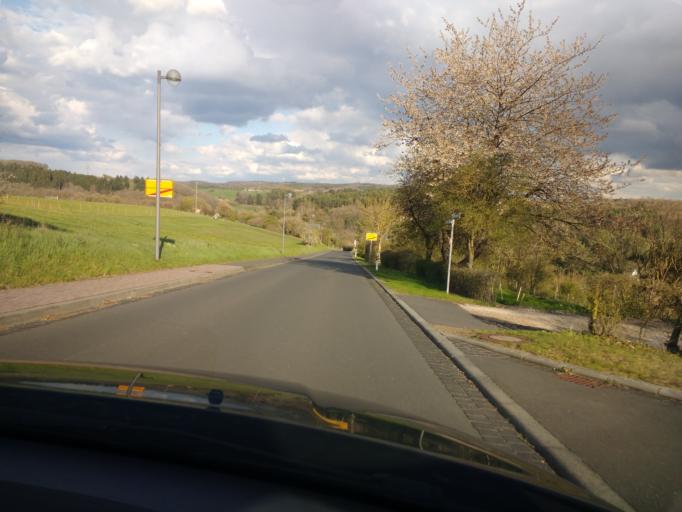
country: DE
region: Rheinland-Pfalz
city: Uxheim
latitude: 50.3397
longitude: 6.7642
